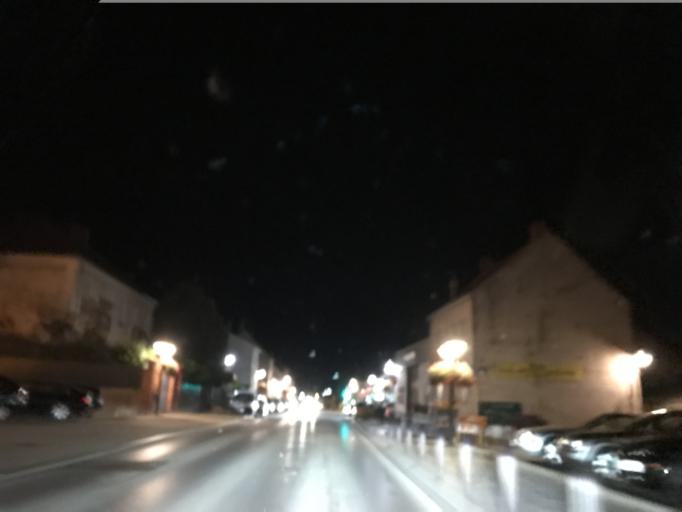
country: FR
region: Auvergne
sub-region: Departement de l'Allier
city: Abrest
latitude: 46.0988
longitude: 3.4449
